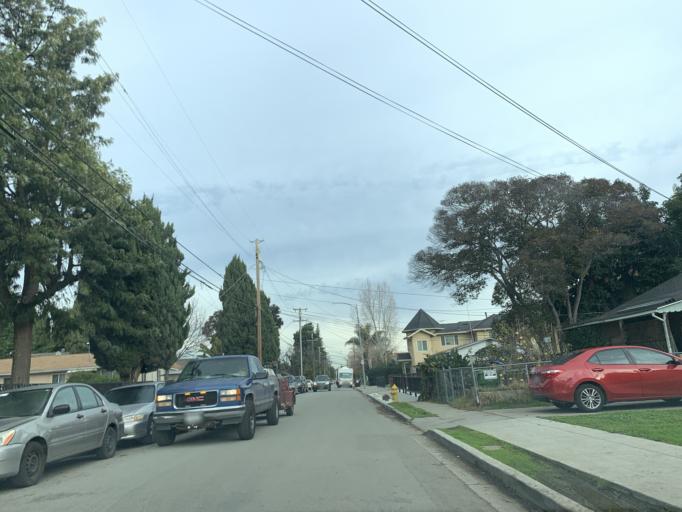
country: US
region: California
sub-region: Santa Clara County
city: Buena Vista
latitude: 37.3193
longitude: -121.9155
